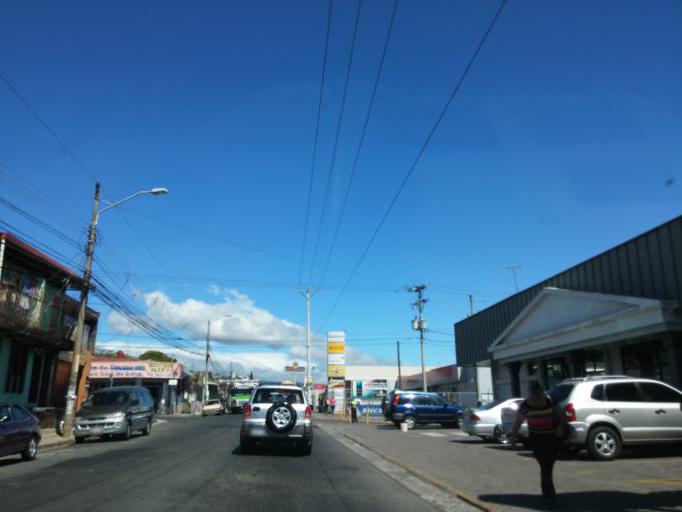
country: CR
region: Alajuela
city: Alajuela
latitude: 10.0142
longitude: -84.2205
